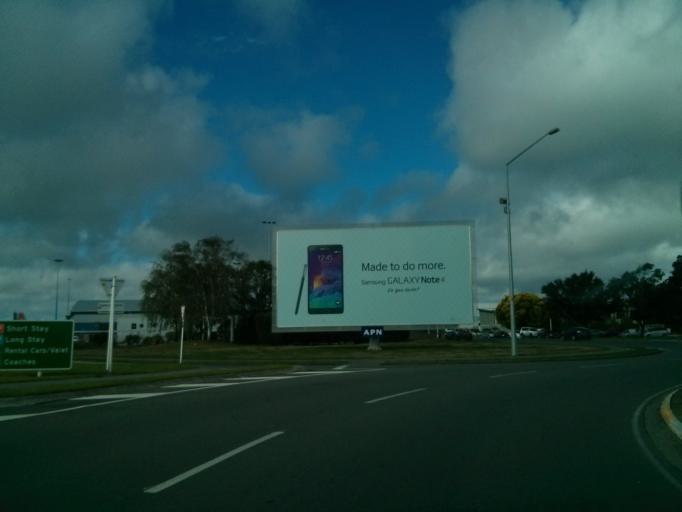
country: NZ
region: Canterbury
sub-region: Selwyn District
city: Prebbleton
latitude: -43.4894
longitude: 172.5444
